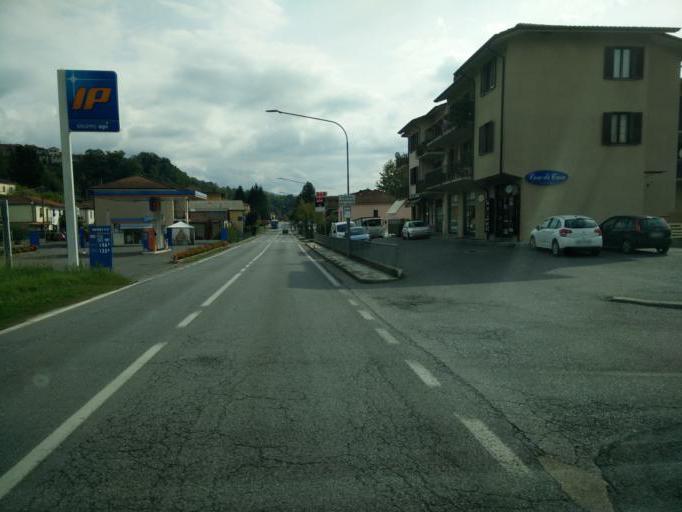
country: IT
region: Tuscany
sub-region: Provincia di Massa-Carrara
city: Filattiera
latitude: 44.3318
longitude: 9.9302
